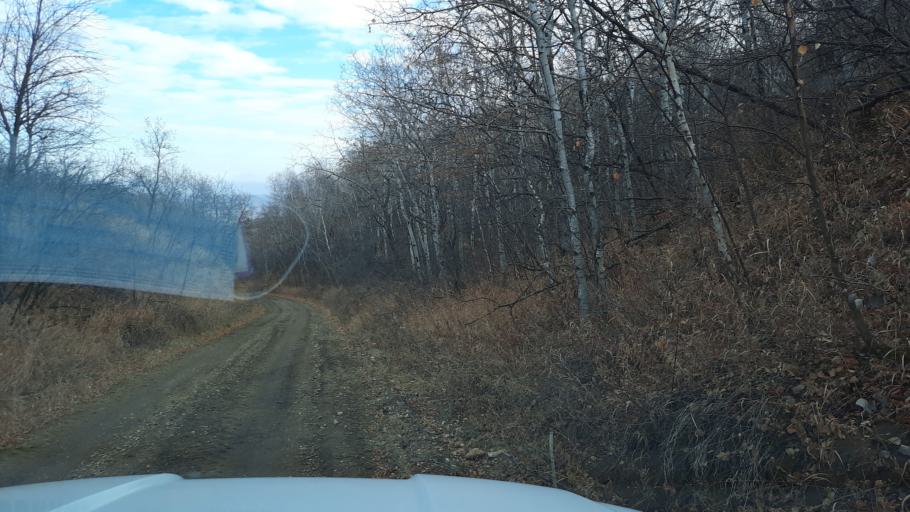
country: CA
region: Saskatchewan
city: Pilot Butte
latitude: 50.7751
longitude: -104.2150
